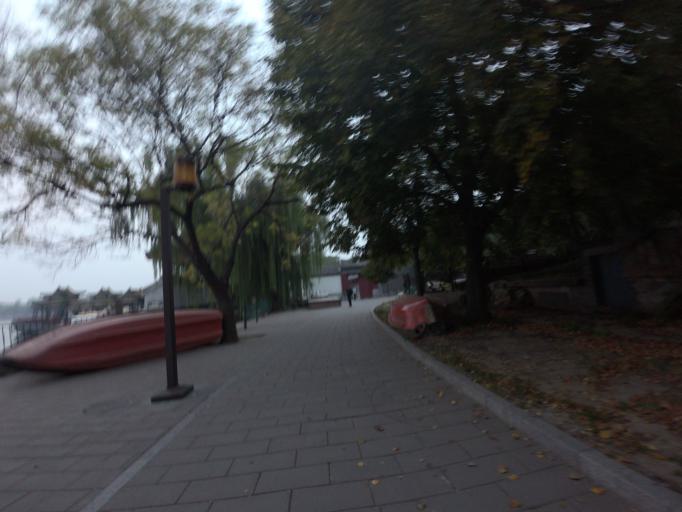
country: CN
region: Beijing
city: Jingshan
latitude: 39.9275
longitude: 116.3854
